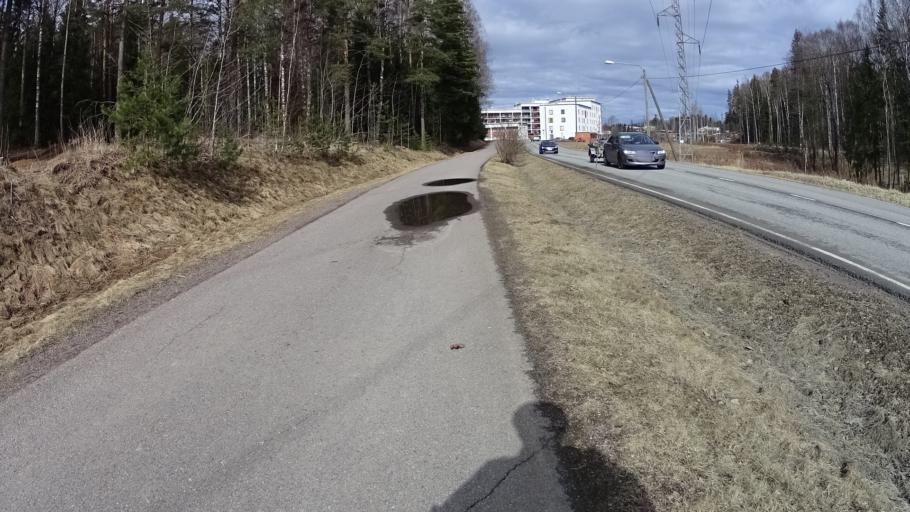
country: FI
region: Uusimaa
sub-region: Helsinki
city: Kilo
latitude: 60.2518
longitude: 24.7992
